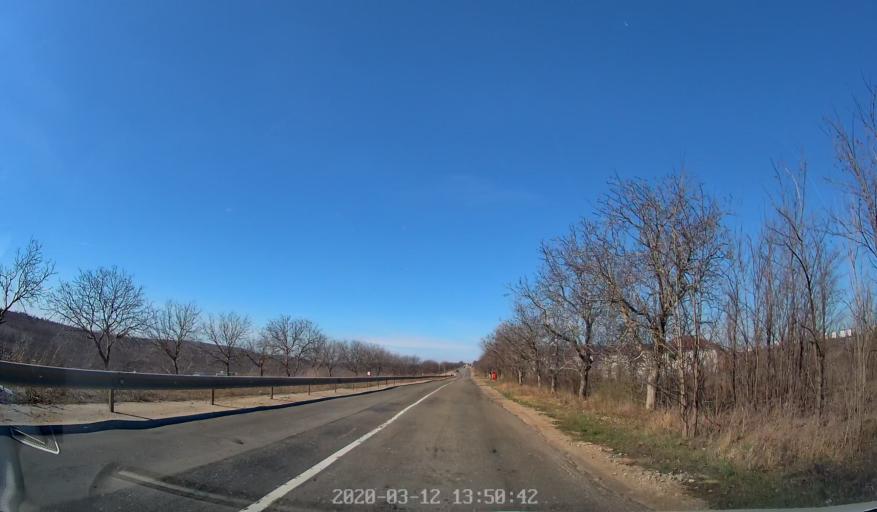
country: MD
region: Laloveni
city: Ialoveni
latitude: 46.9901
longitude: 28.7413
